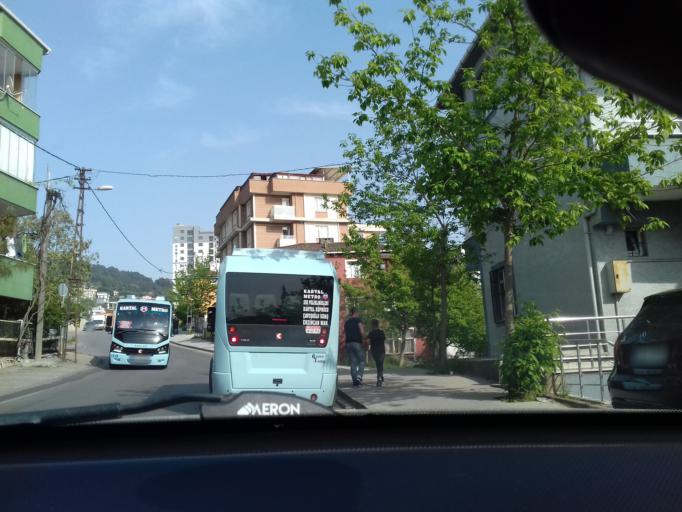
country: TR
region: Istanbul
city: Pendik
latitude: 40.9123
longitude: 29.2286
